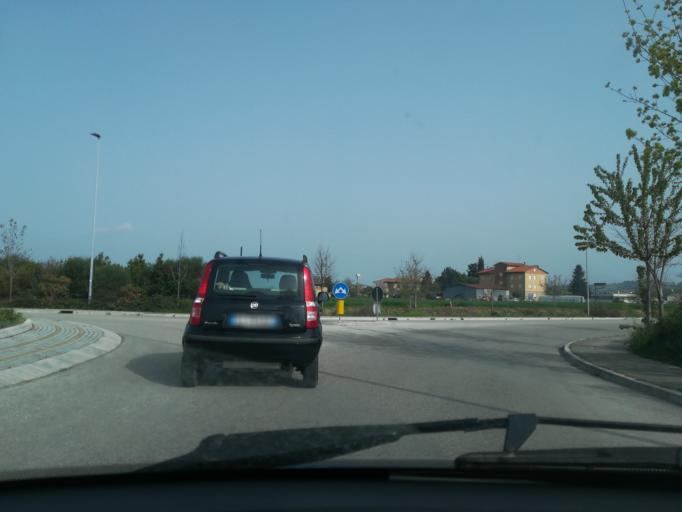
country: IT
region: The Marches
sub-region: Provincia di Macerata
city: Piediripa
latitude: 43.2827
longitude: 13.4967
